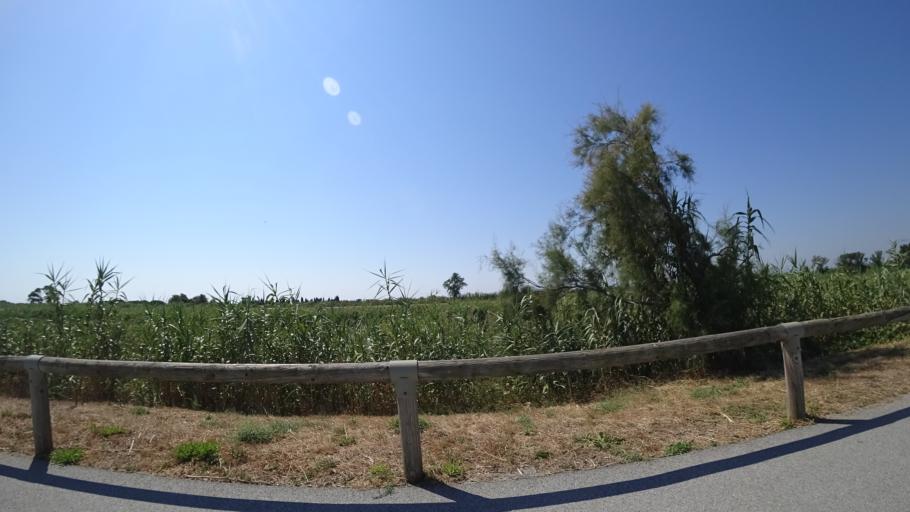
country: FR
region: Languedoc-Roussillon
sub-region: Departement des Pyrenees-Orientales
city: Saint-Laurent-de-la-Salanque
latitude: 42.7701
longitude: 3.0113
